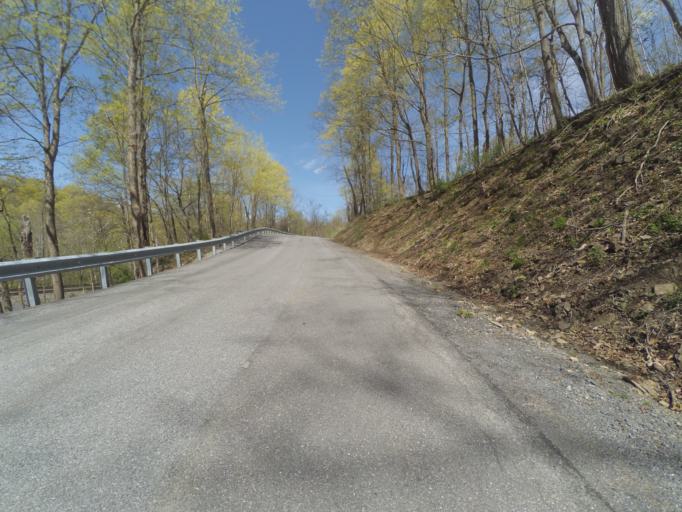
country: US
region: Pennsylvania
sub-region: Blair County
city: Tyrone
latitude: 40.6136
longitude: -78.1523
